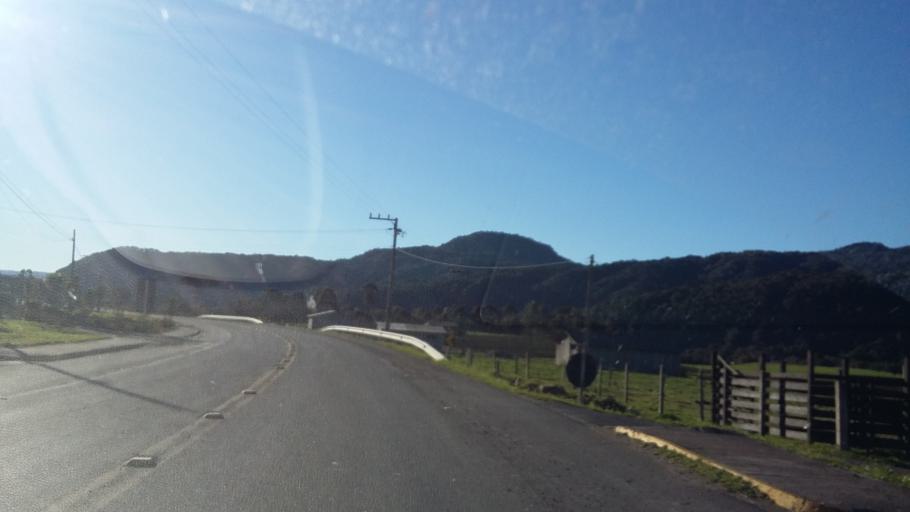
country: BR
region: Santa Catarina
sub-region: Lauro Muller
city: Lauro Muller
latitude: -28.0224
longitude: -49.5003
